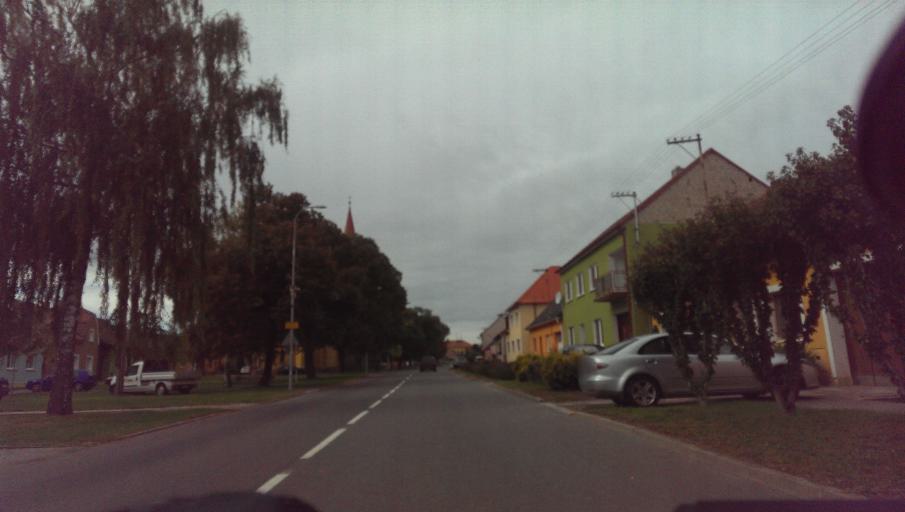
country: CZ
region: South Moravian
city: Moravsky Pisek
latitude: 48.9896
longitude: 17.3380
